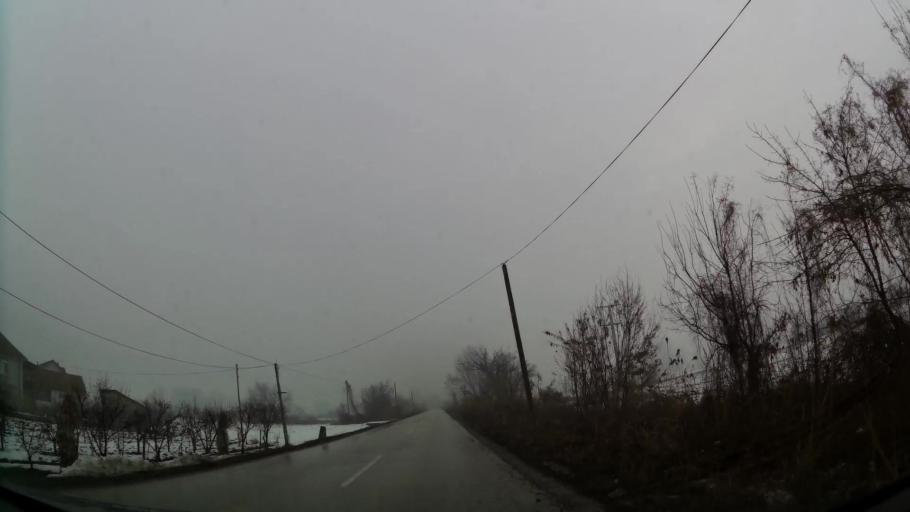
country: MK
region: Ilinden
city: Idrizovo
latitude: 41.9481
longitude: 21.5916
